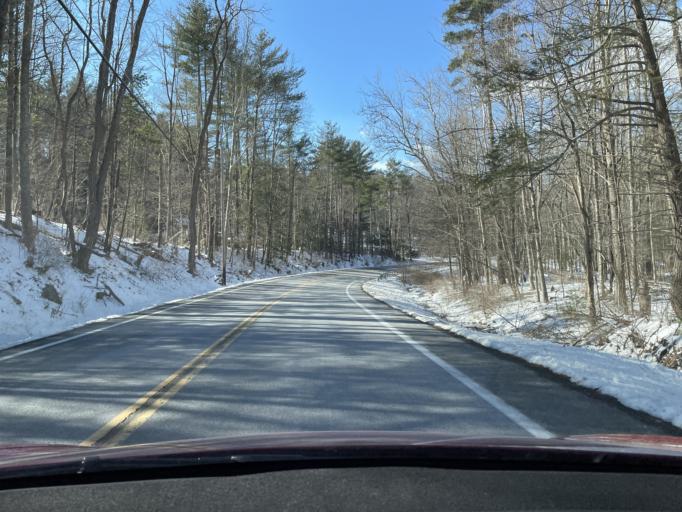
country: US
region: New York
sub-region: Ulster County
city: Shokan
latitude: 42.0523
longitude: -74.2626
